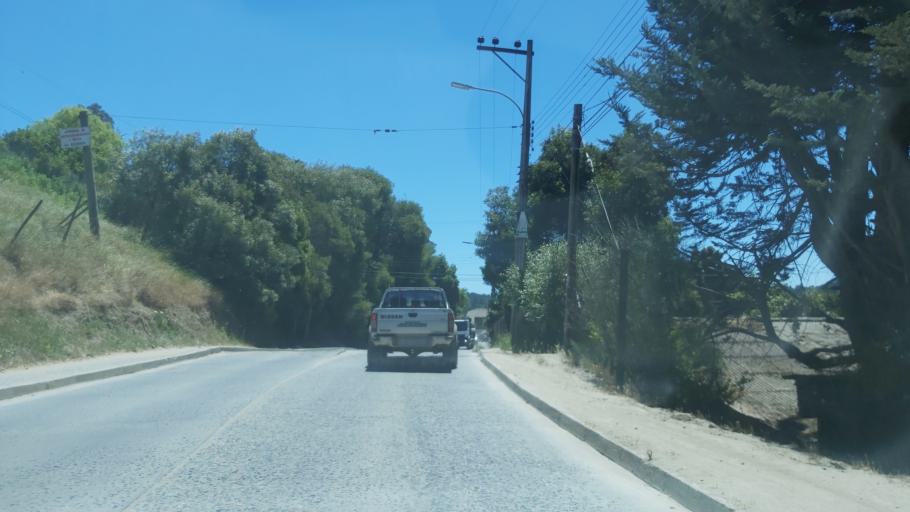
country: CL
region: Maule
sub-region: Provincia de Talca
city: Constitucion
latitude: -35.3419
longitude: -72.3966
